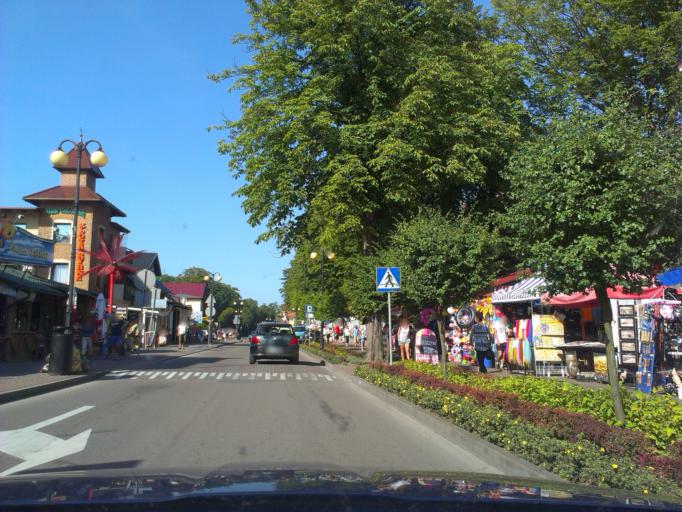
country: PL
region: West Pomeranian Voivodeship
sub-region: Powiat kamienski
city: Dziwnow
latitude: 54.0249
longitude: 14.7534
